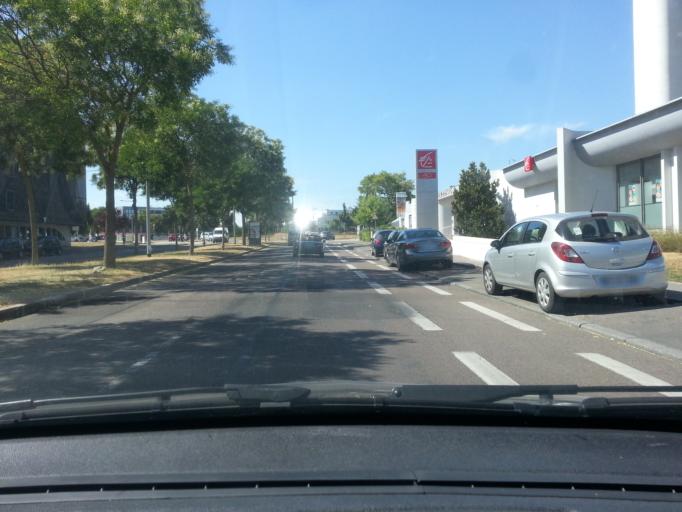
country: FR
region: Bourgogne
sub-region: Departement de la Cote-d'Or
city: Fontaine-les-Dijon
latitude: 47.3462
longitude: 5.0467
